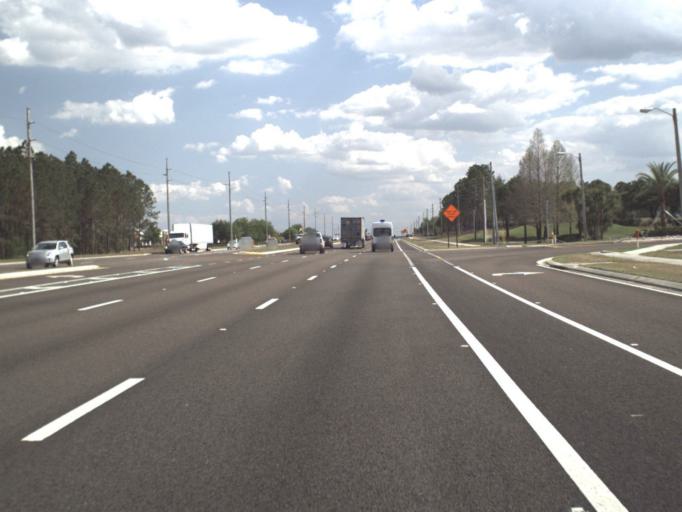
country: US
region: Florida
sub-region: Lake County
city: Clermont
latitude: 28.5058
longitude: -81.7213
